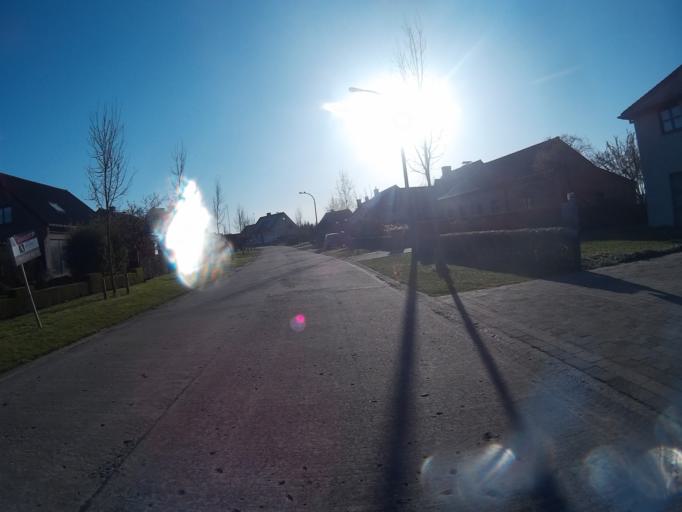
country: BE
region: Flanders
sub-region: Provincie Oost-Vlaanderen
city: Aalter
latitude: 51.0917
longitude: 3.4573
